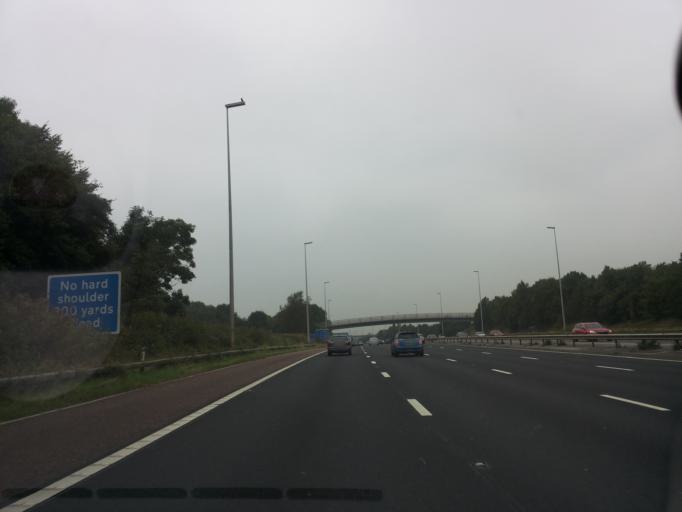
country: GB
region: England
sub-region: Lancashire
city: Goosnargh
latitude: 53.7962
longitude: -2.6801
